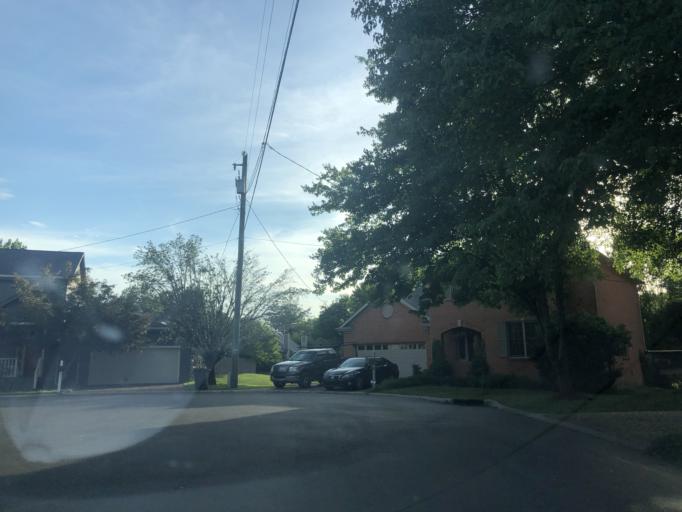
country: US
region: Tennessee
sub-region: Davidson County
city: Belle Meade
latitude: 36.0678
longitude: -86.9401
